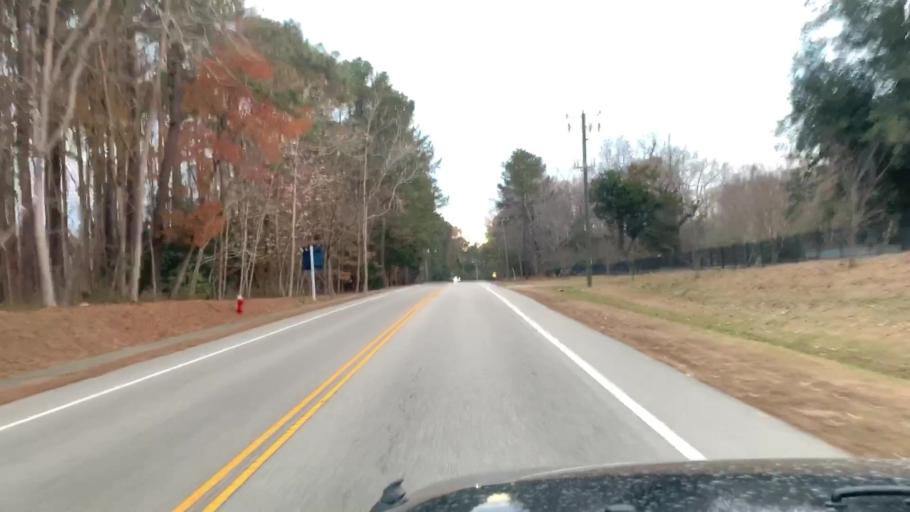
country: US
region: Virginia
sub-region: City of Williamsburg
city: Williamsburg
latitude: 37.2555
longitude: -76.7104
